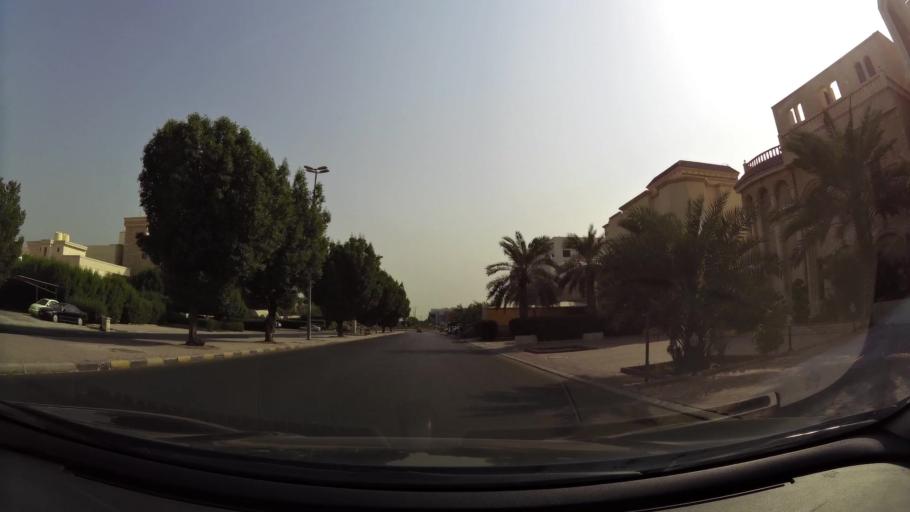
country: KW
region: Mubarak al Kabir
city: Sabah as Salim
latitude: 29.2790
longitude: 48.0531
